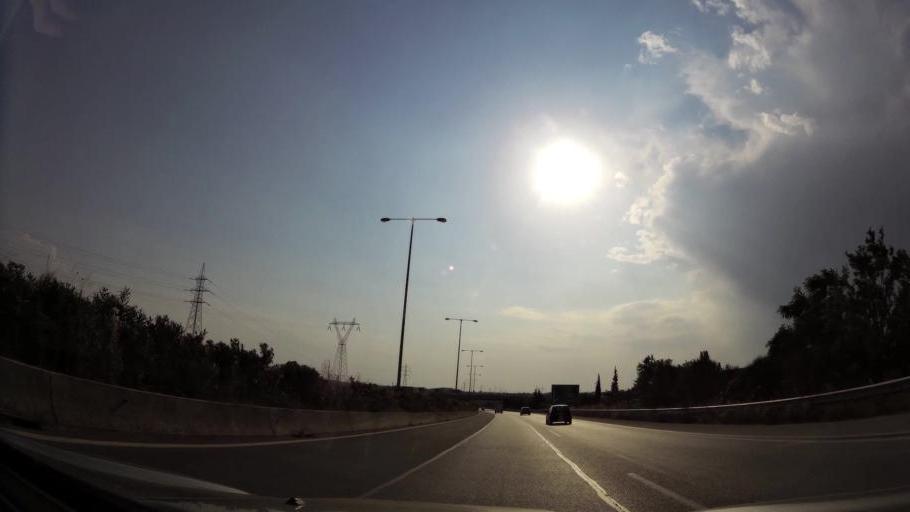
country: GR
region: Central Macedonia
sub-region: Nomos Thessalonikis
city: Diavata
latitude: 40.6971
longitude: 22.8582
